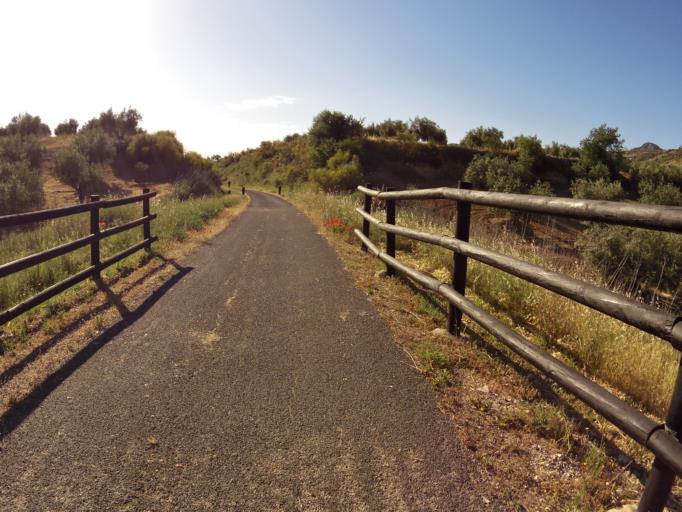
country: ES
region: Andalusia
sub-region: Province of Cordoba
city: Luque
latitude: 37.5650
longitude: -4.2449
